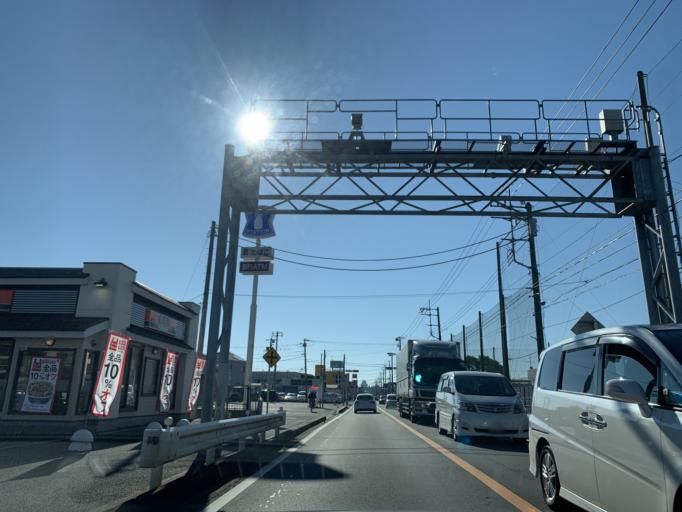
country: JP
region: Chiba
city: Matsudo
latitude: 35.8048
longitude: 139.8951
